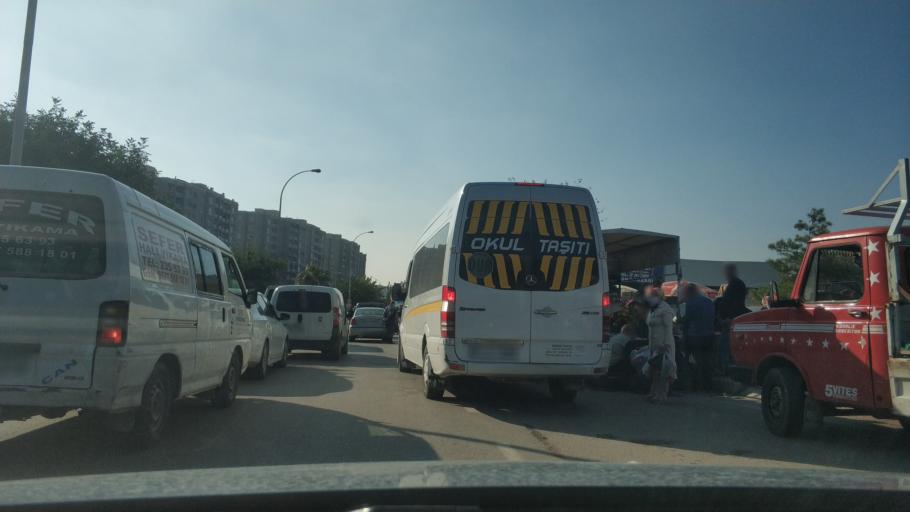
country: TR
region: Adana
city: Seyhan
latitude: 37.0123
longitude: 35.2808
